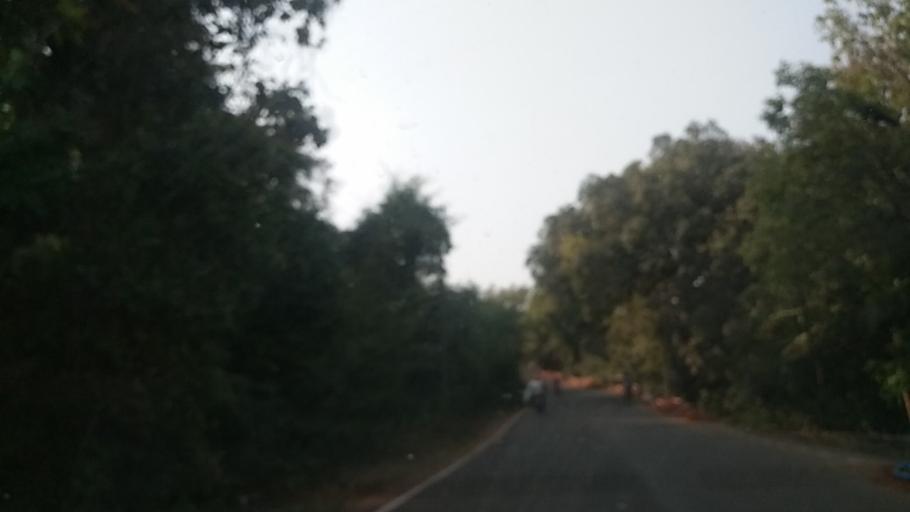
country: IN
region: Goa
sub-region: North Goa
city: Pernem
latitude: 15.7151
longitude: 73.8056
